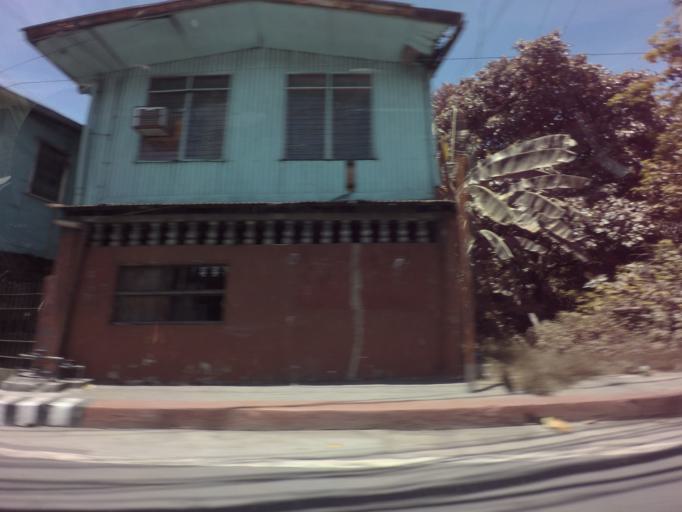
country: PH
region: Calabarzon
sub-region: Province of Rizal
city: Las Pinas
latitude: 14.4756
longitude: 120.9783
